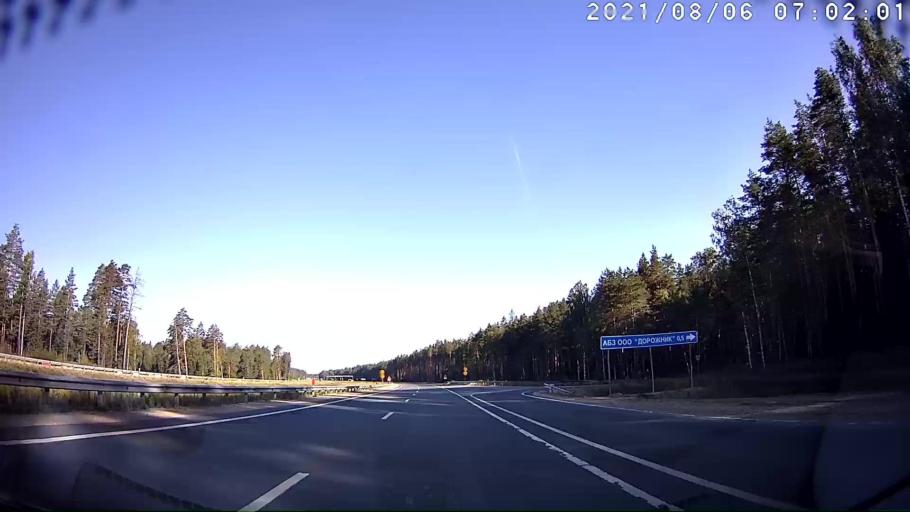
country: RU
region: Mariy-El
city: Surok
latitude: 56.5299
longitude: 48.0031
